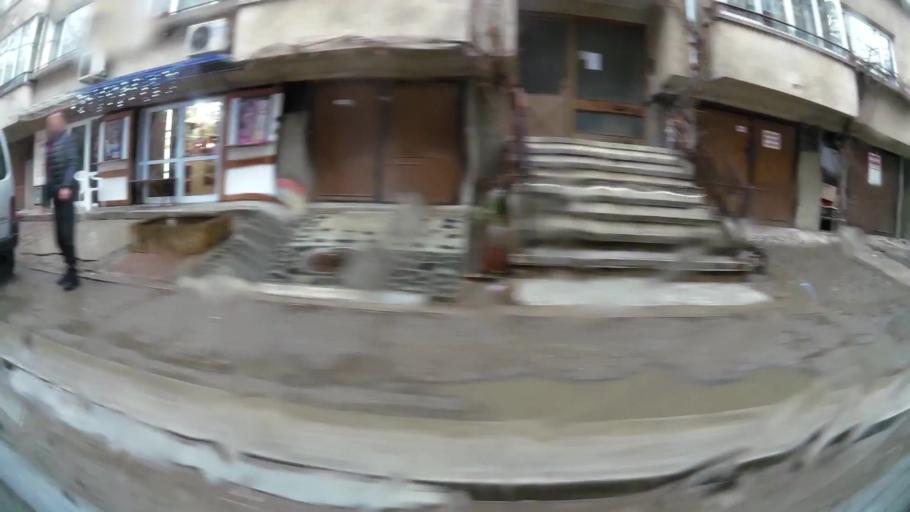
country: BG
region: Sofia-Capital
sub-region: Stolichna Obshtina
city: Sofia
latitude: 42.6536
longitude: 23.3634
